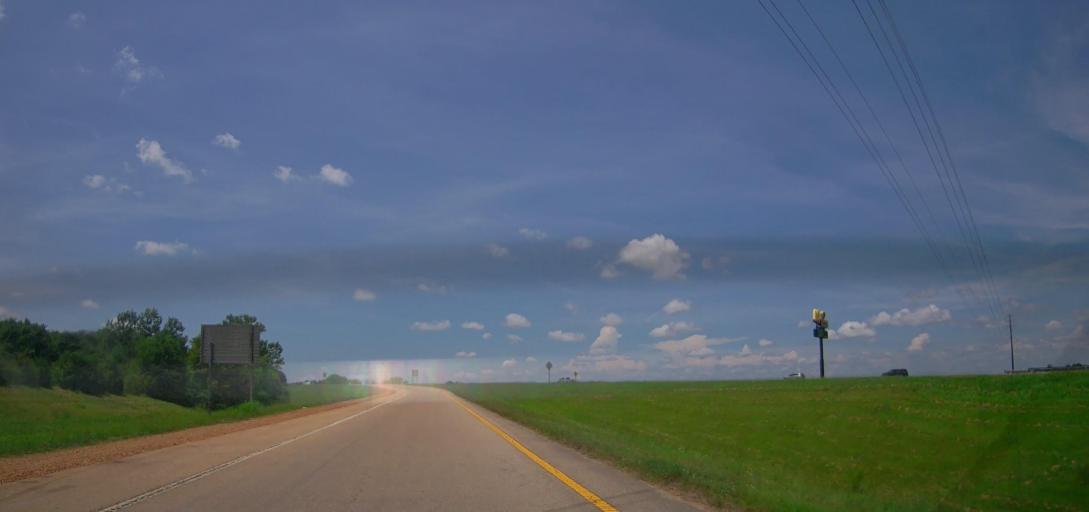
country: US
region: Mississippi
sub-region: Lee County
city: Tupelo
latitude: 34.3130
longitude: -88.7903
